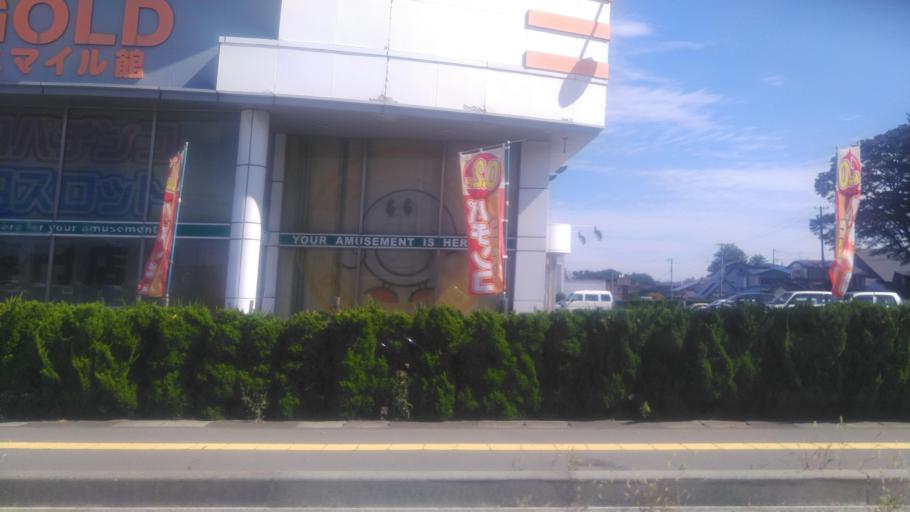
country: JP
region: Akita
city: Noshiromachi
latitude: 40.1959
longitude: 140.0227
